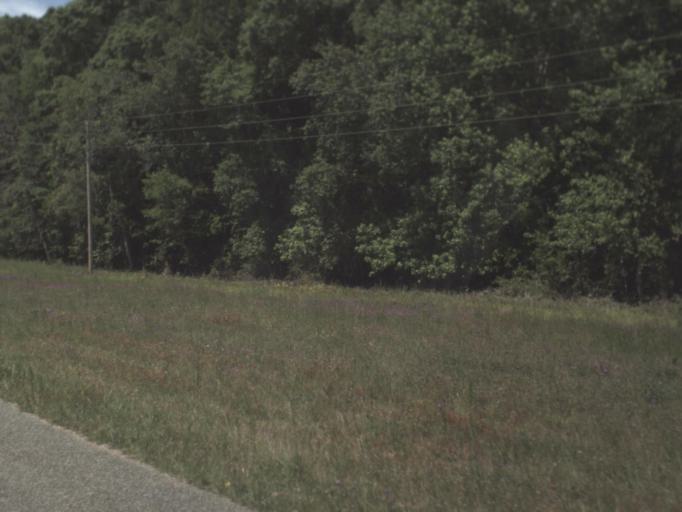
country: US
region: Florida
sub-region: Jackson County
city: Marianna
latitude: 30.6909
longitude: -85.2354
